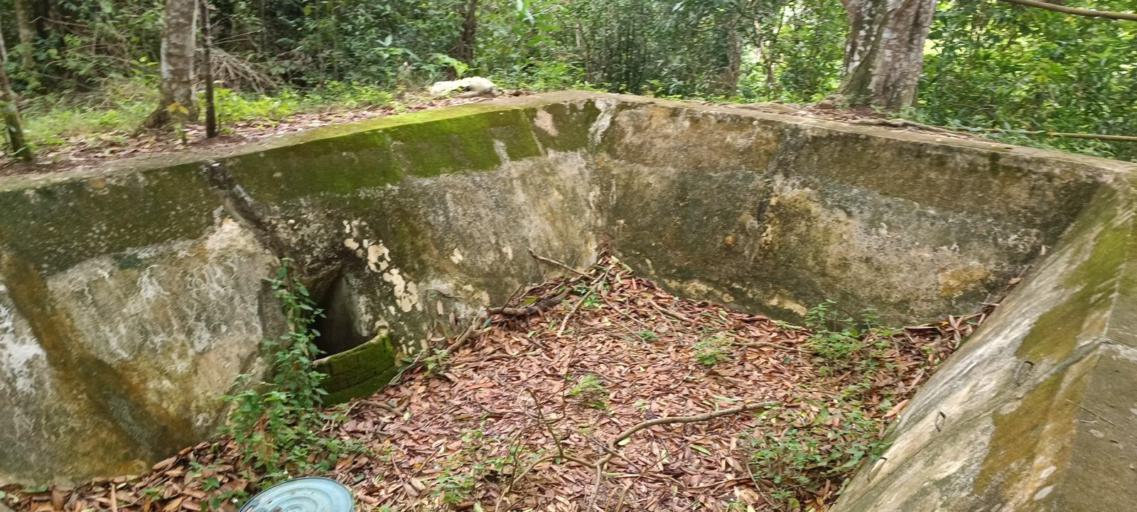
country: MY
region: Penang
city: George Town
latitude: 5.3838
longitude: 100.2881
